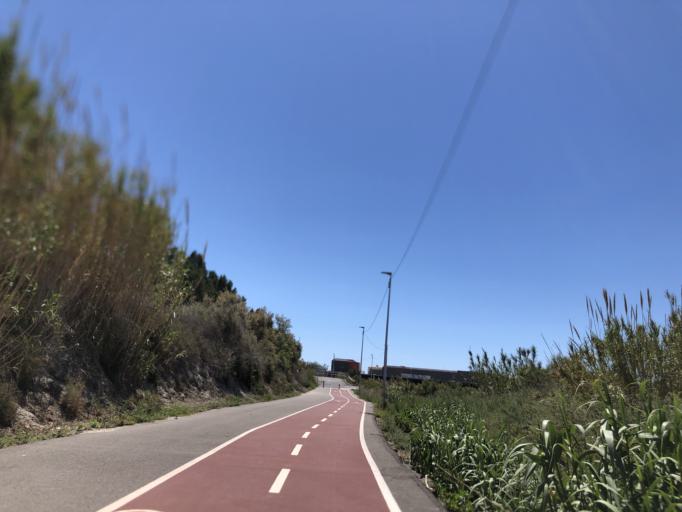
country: ES
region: Andalusia
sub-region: Provincia de Almeria
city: Almeria
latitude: 36.8337
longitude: -2.4029
